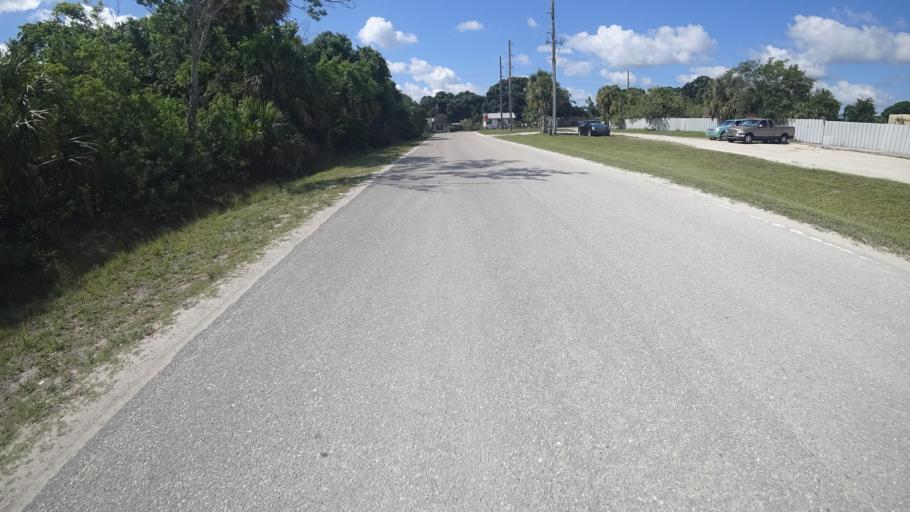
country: US
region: Florida
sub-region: Manatee County
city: Whitfield
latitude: 27.4151
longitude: -82.5282
